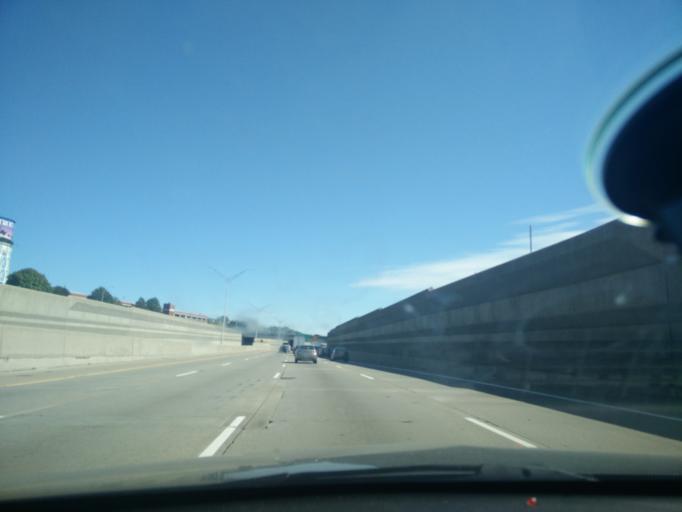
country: US
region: Michigan
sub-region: Oakland County
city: Pleasant Ridge
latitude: 42.4746
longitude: -83.1508
